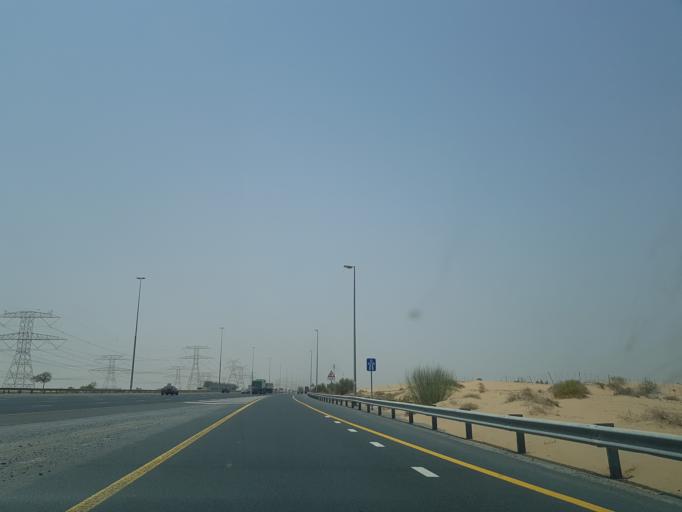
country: AE
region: Ash Shariqah
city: Sharjah
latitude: 25.1225
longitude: 55.4426
